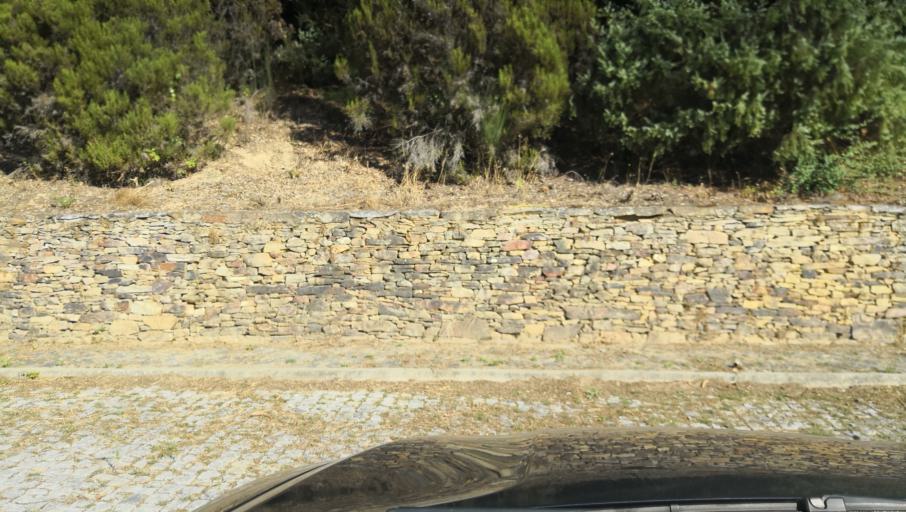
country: PT
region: Vila Real
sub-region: Vila Real
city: Vila Real
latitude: 41.2835
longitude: -7.7463
